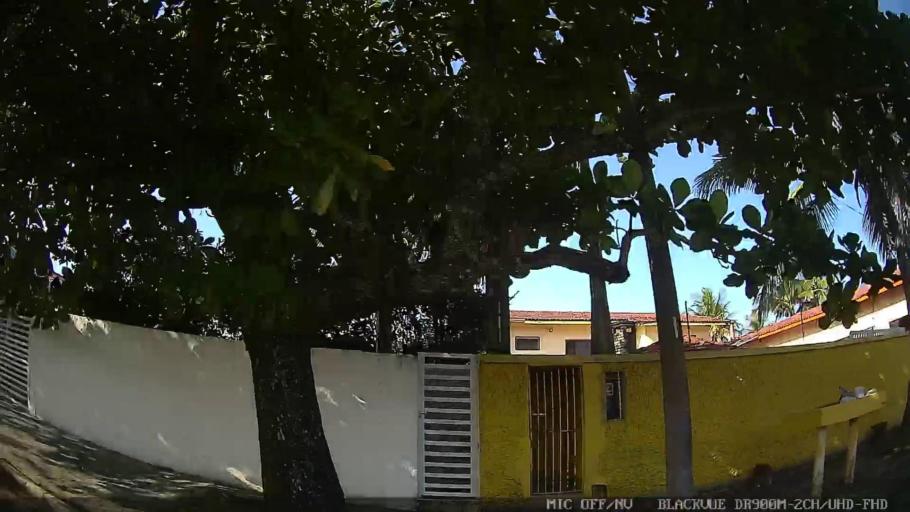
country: BR
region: Sao Paulo
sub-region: Peruibe
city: Peruibe
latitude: -24.2927
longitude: -46.9599
